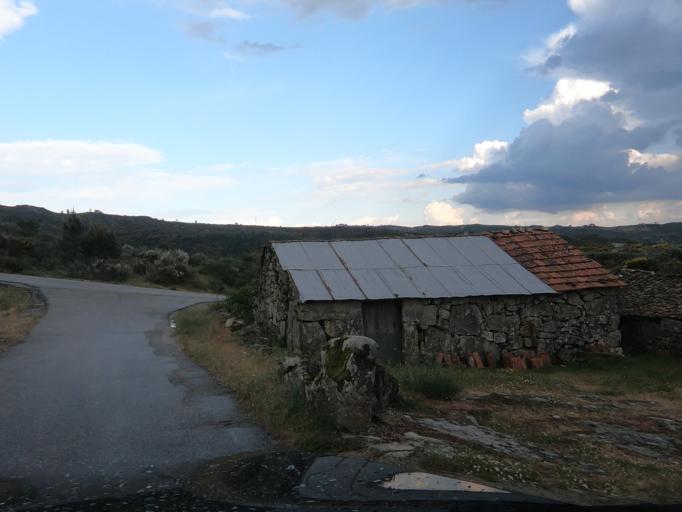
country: PT
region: Vila Real
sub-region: Vila Real
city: Vila Real
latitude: 41.3690
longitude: -7.7148
